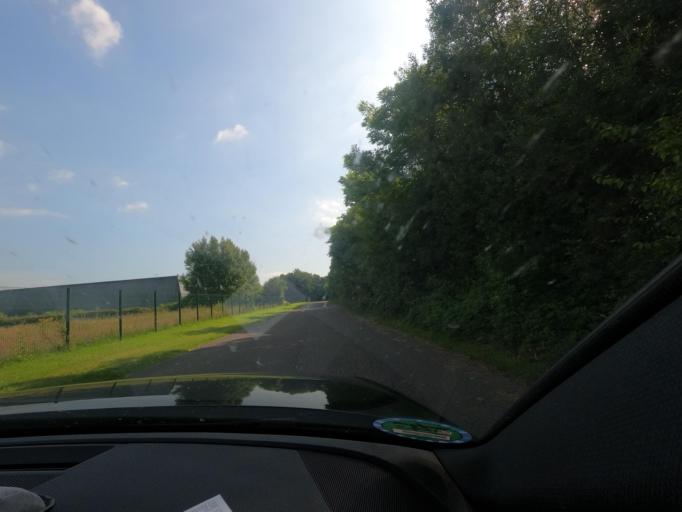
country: FR
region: Lower Normandy
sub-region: Departement du Calvados
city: La Riviere-Saint-Sauveur
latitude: 49.3946
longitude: 0.2559
